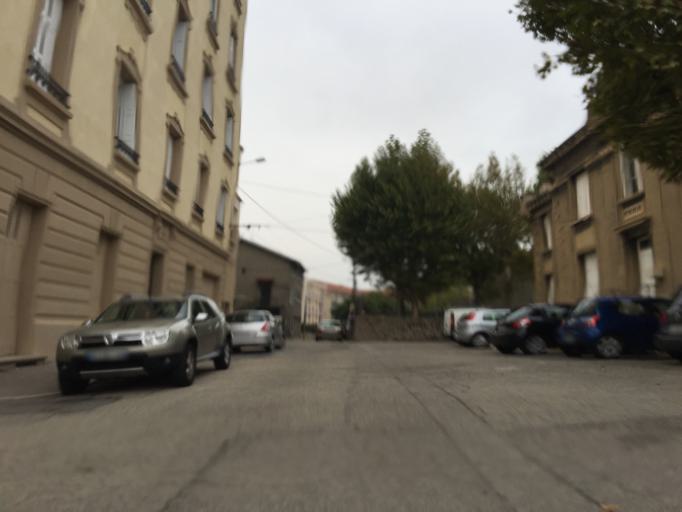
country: FR
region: Rhone-Alpes
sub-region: Departement de la Loire
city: Saint-Chamond
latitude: 45.4723
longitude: 4.5127
